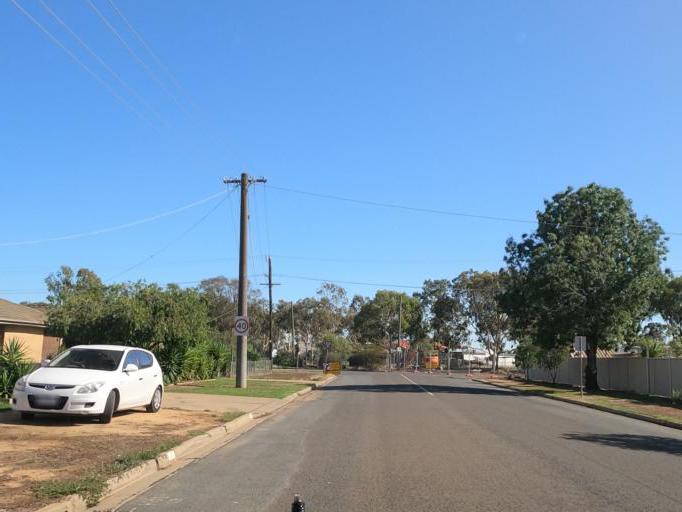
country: AU
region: Victoria
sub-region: Moira
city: Yarrawonga
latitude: -36.0226
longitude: 146.0087
